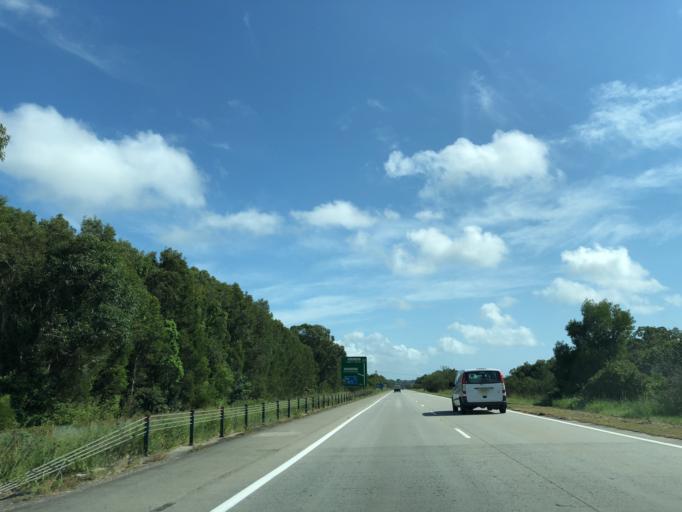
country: AU
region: New South Wales
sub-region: Byron Shire
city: Brunswick Heads
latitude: -28.5974
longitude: 153.5447
